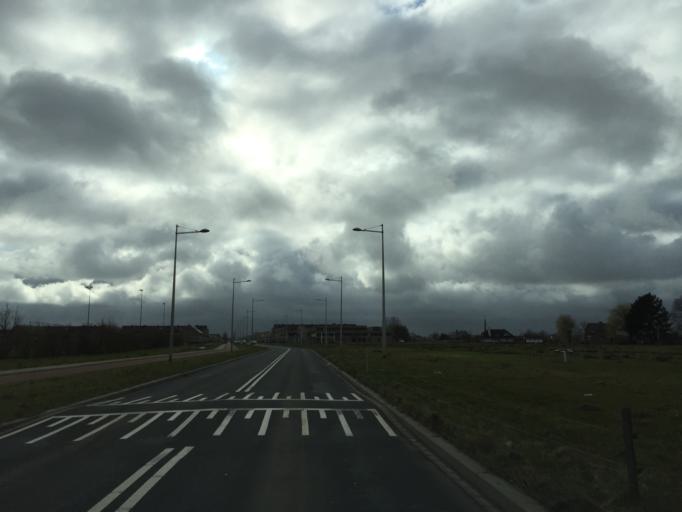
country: NL
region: South Holland
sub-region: Gemeente Lansingerland
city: Berkel en Rodenrijs
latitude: 52.0031
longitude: 4.4728
